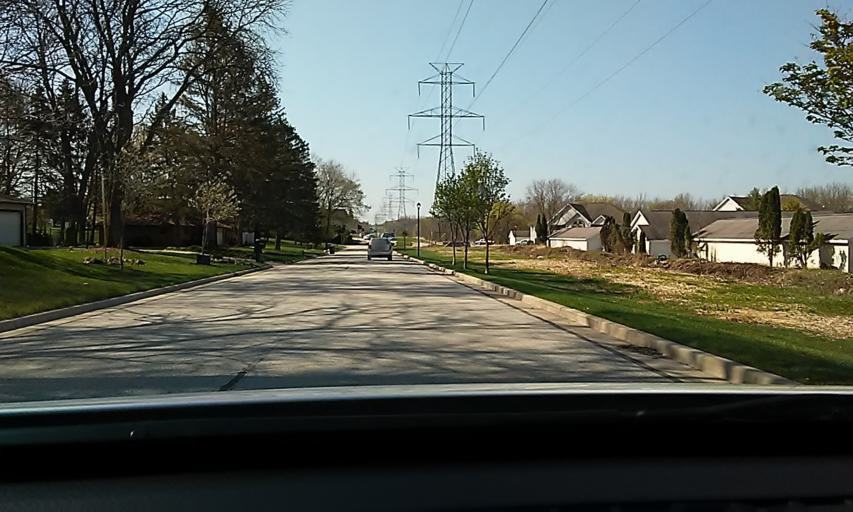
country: US
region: Wisconsin
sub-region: Milwaukee County
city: Greenfield
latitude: 42.9803
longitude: -88.0508
